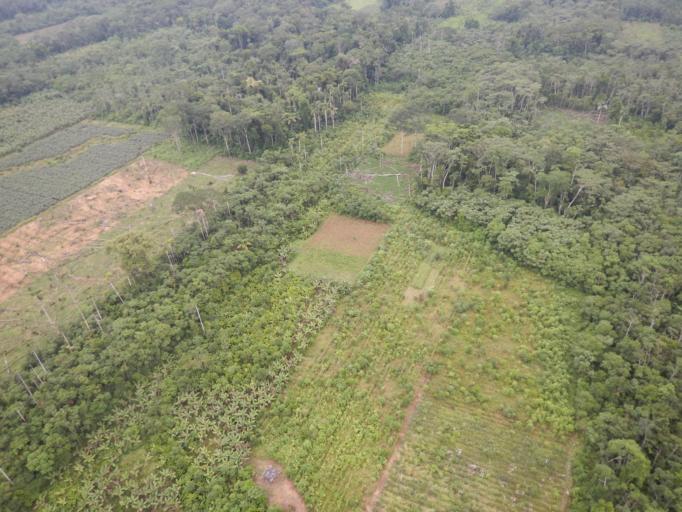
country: BO
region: Cochabamba
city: Chimore
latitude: -17.1502
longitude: -64.7973
